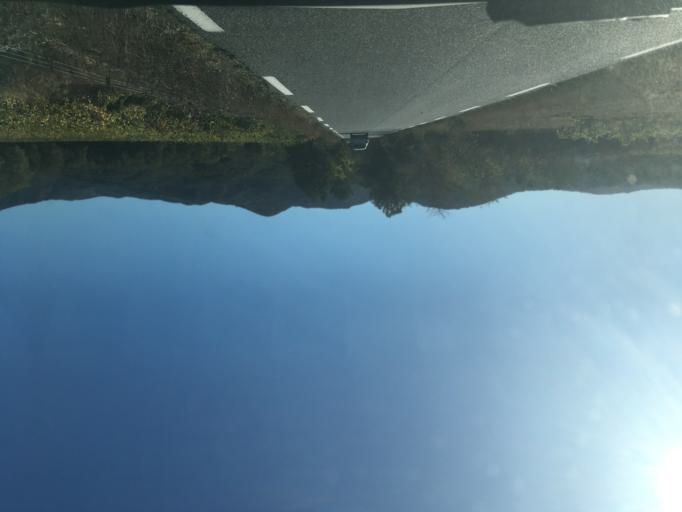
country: FR
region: Provence-Alpes-Cote d'Azur
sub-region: Departement du Var
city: La Garde-Freinet
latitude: 43.3391
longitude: 6.4275
